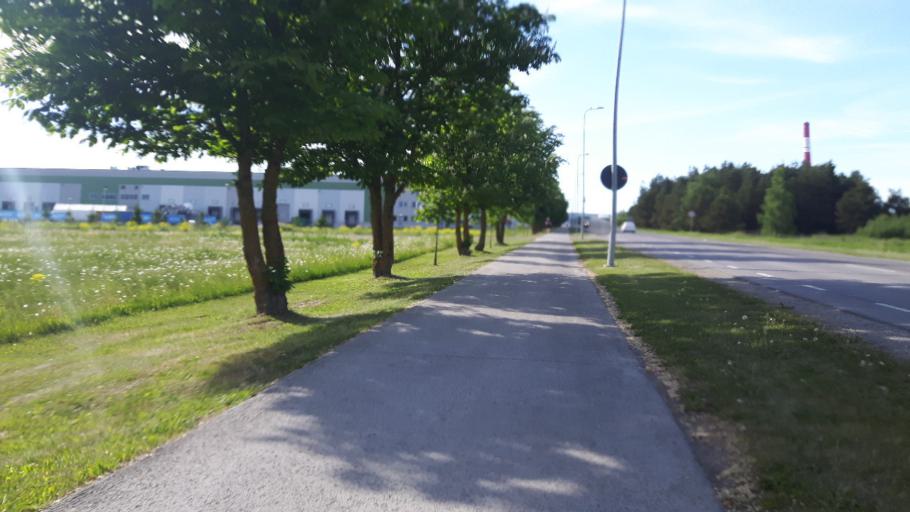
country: EE
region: Harju
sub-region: Joelaehtme vald
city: Loo
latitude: 59.4395
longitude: 24.9362
